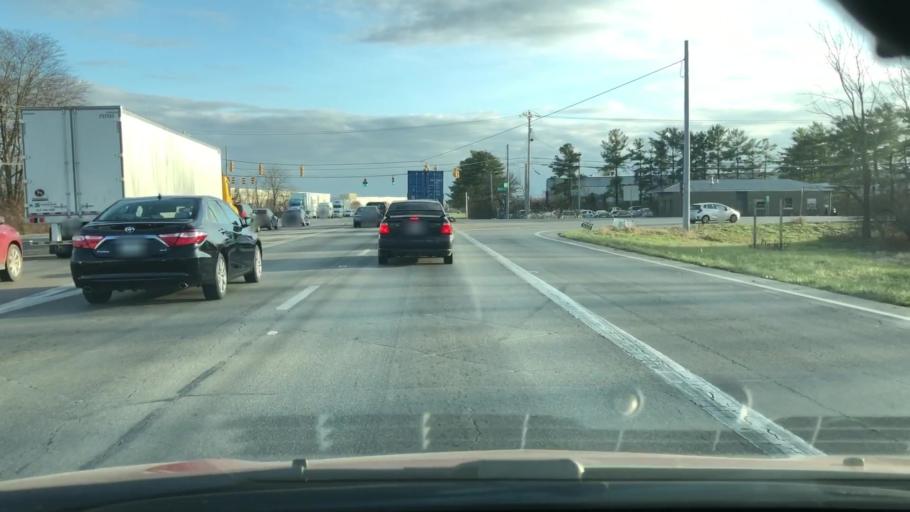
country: US
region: Ohio
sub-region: Franklin County
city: Obetz
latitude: 39.8447
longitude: -82.9365
